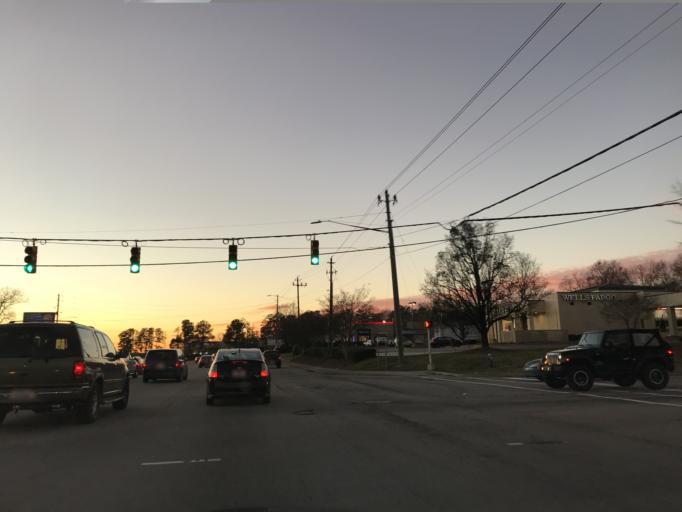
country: US
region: North Carolina
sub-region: Wake County
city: Raleigh
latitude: 35.7992
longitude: -78.5681
